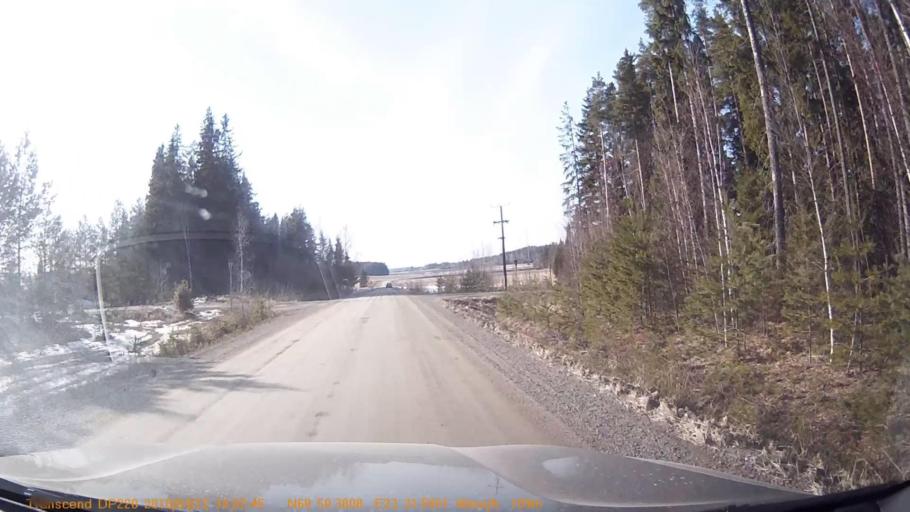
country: FI
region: Haeme
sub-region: Forssa
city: Jokioinen
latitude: 60.8395
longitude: 23.5267
